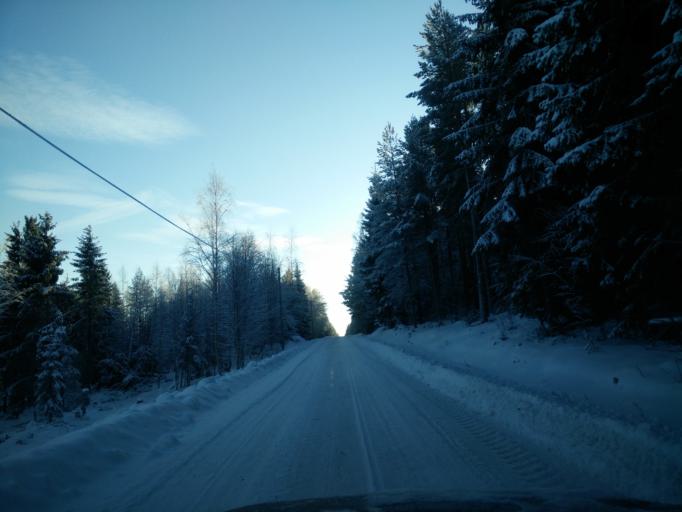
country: SE
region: Vaesternorrland
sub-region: Sundsvalls Kommun
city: Njurundabommen
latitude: 62.2186
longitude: 17.4934
